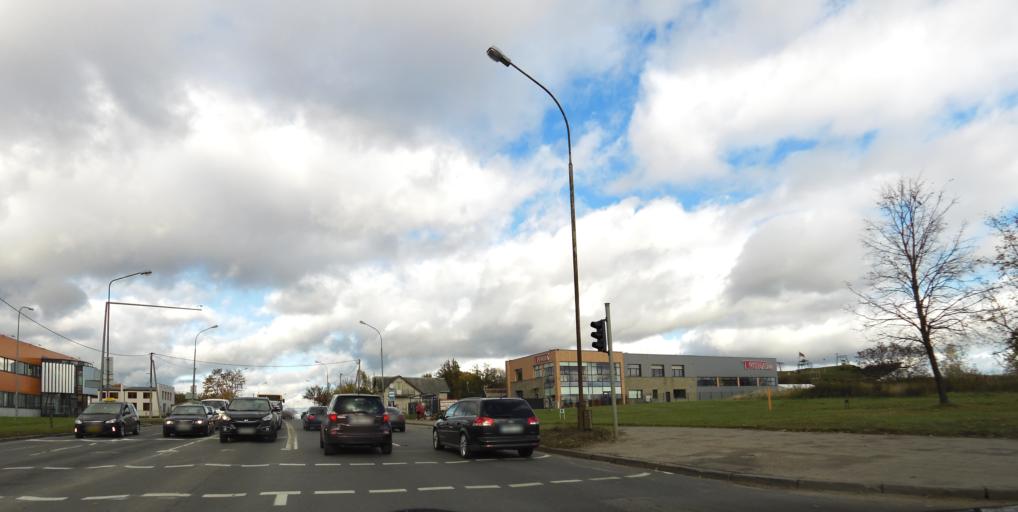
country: LT
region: Vilnius County
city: Rasos
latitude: 54.6543
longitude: 25.3029
